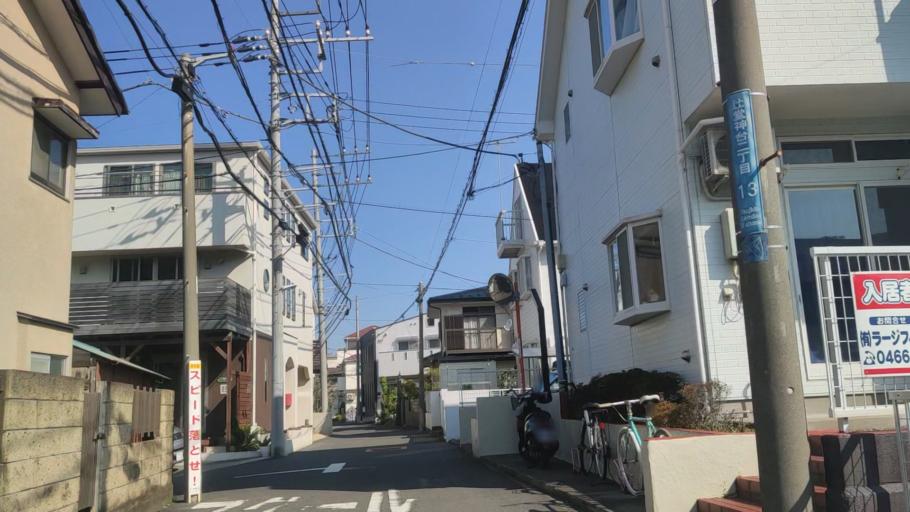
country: JP
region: Kanagawa
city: Fujisawa
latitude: 35.3424
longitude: 139.4435
